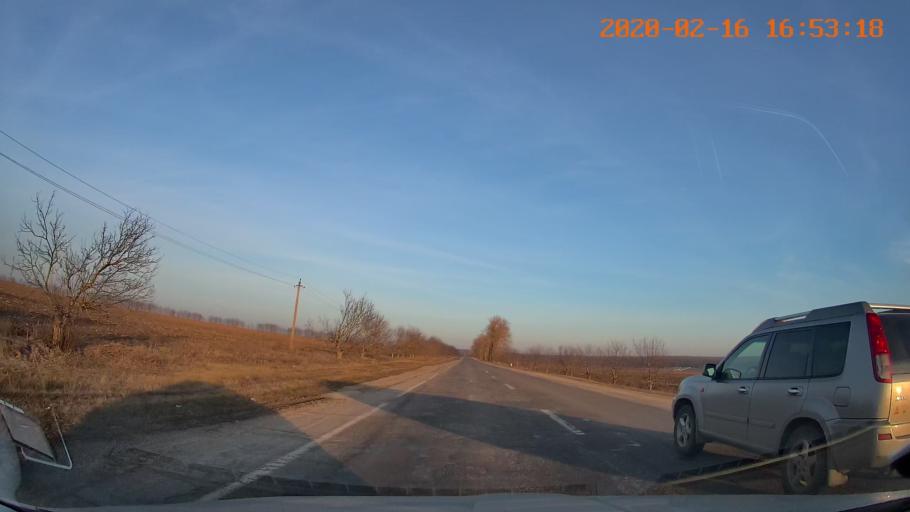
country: MD
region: Briceni
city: Briceni
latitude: 48.3165
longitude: 26.9799
